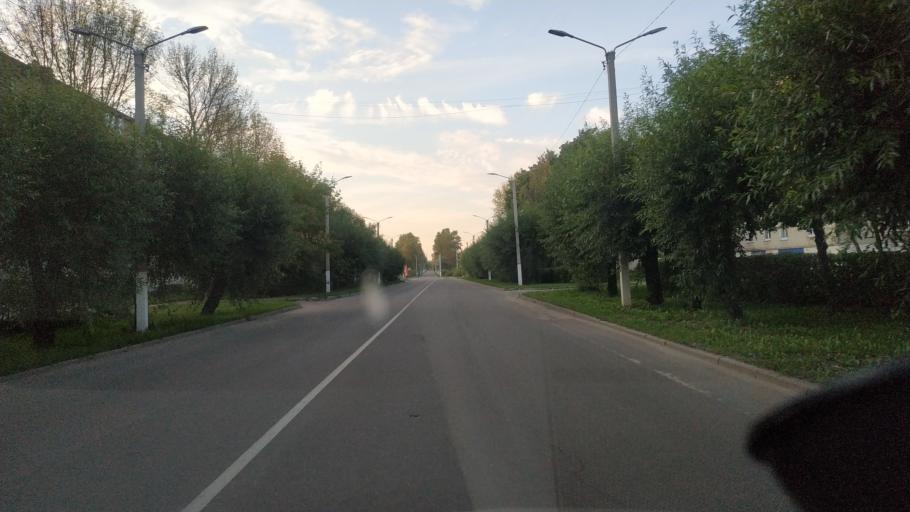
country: RU
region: Moskovskaya
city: Roshal'
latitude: 55.6648
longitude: 39.8526
